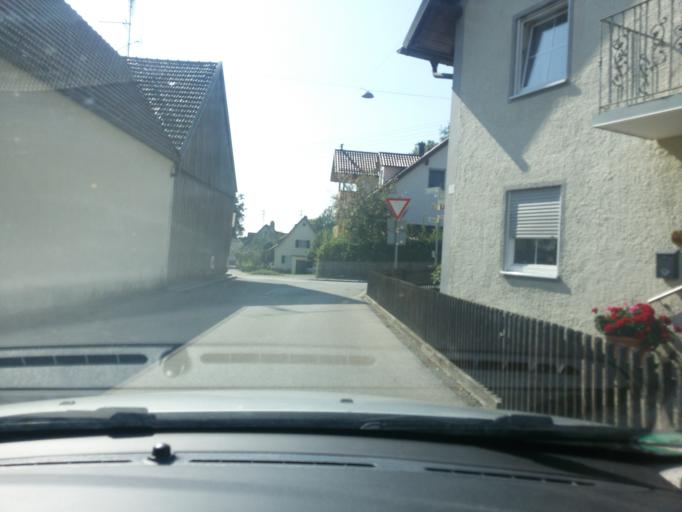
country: DE
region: Bavaria
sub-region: Swabia
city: Hiltenfingen
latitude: 48.1861
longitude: 10.6897
